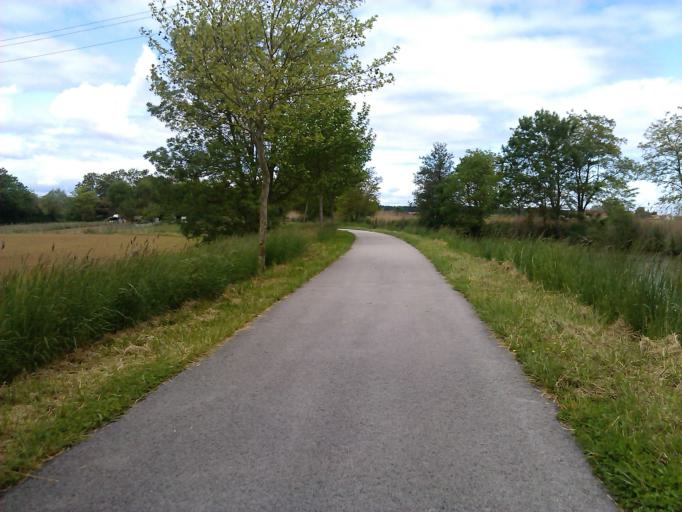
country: FR
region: Bourgogne
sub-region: Departement de Saone-et-Loire
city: Champforgeuil
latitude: 46.8375
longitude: 4.8298
